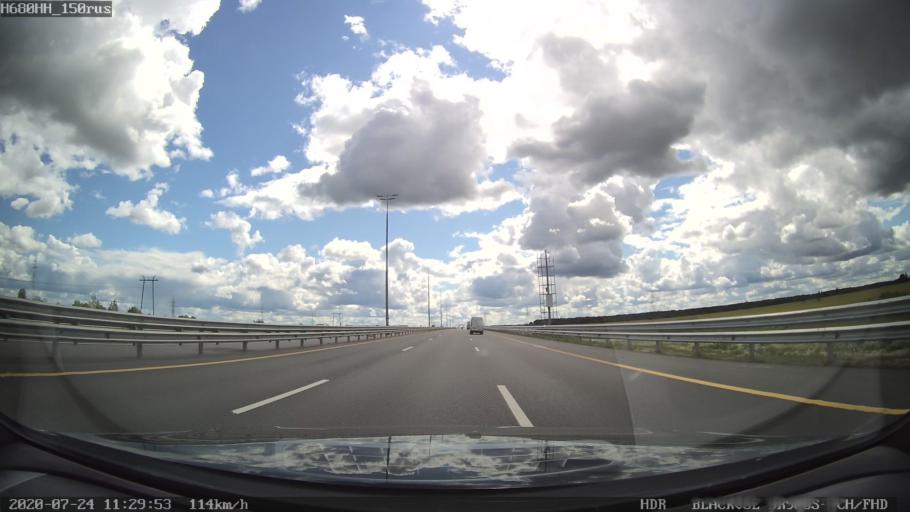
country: RU
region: Leningrad
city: Krasnyy Bor
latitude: 59.6760
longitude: 30.6011
